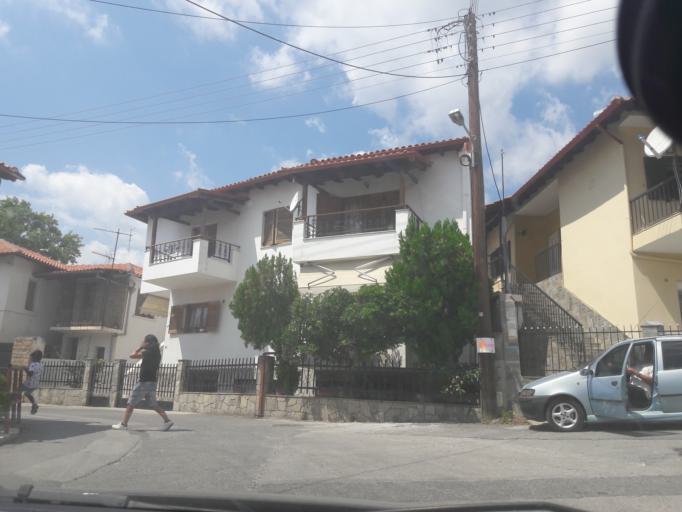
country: GR
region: Central Macedonia
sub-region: Nomos Chalkidikis
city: Polygyros
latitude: 40.3765
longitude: 23.4391
